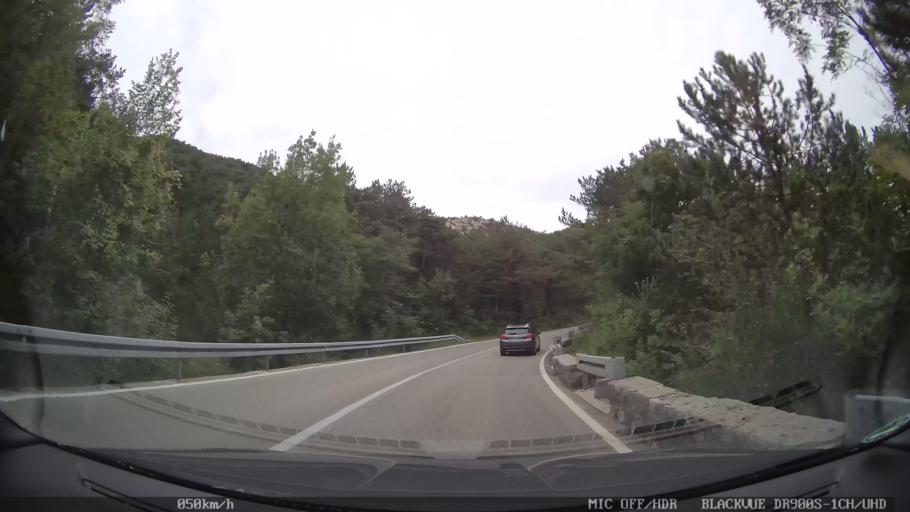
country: HR
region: Primorsko-Goranska
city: Punat
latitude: 45.0233
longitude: 14.6775
